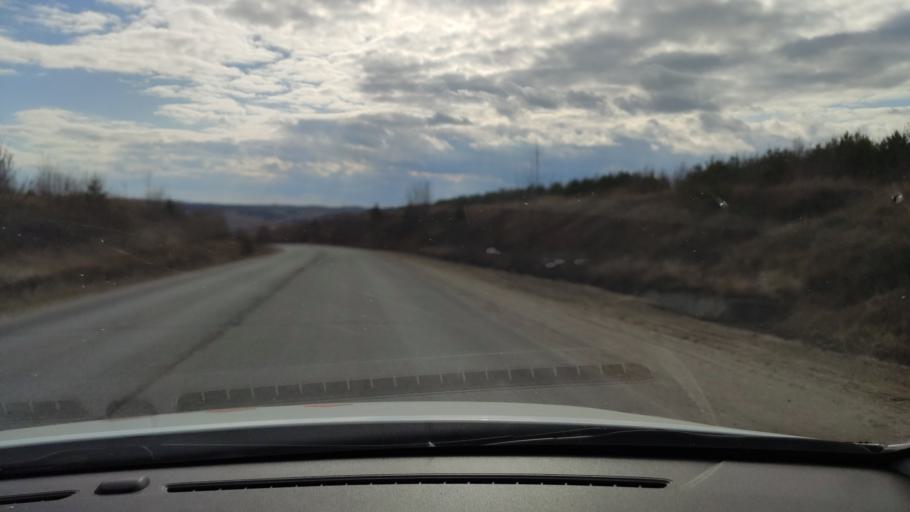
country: RU
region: Tatarstan
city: Vysokaya Gora
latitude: 56.0349
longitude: 49.2140
